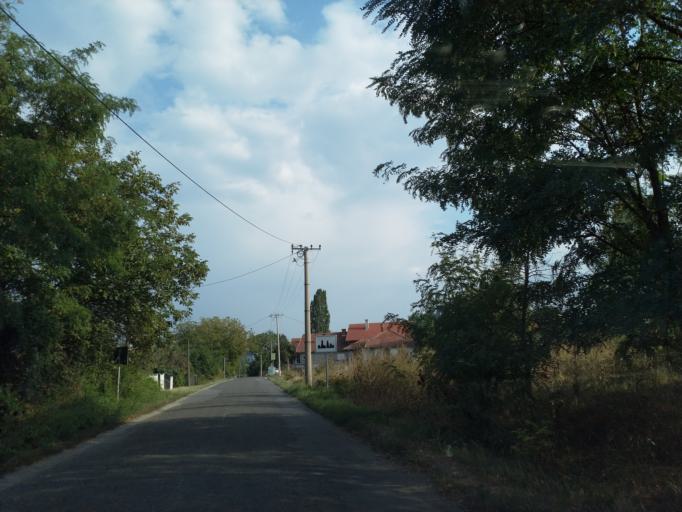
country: RS
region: Central Serbia
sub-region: Pomoravski Okrug
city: Paracin
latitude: 43.8437
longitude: 21.4707
